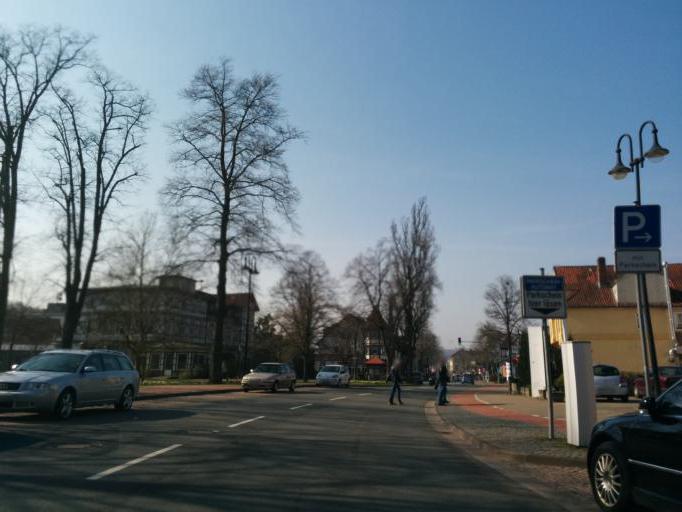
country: DE
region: Lower Saxony
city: Bad Lauterberg im Harz
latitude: 51.6307
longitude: 10.4704
